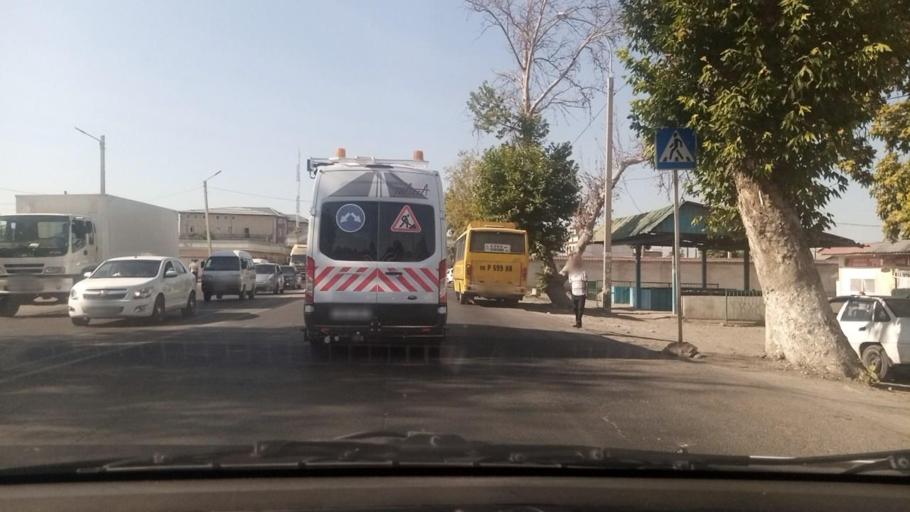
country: UZ
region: Toshkent Shahri
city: Bektemir
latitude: 41.2271
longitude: 69.3356
